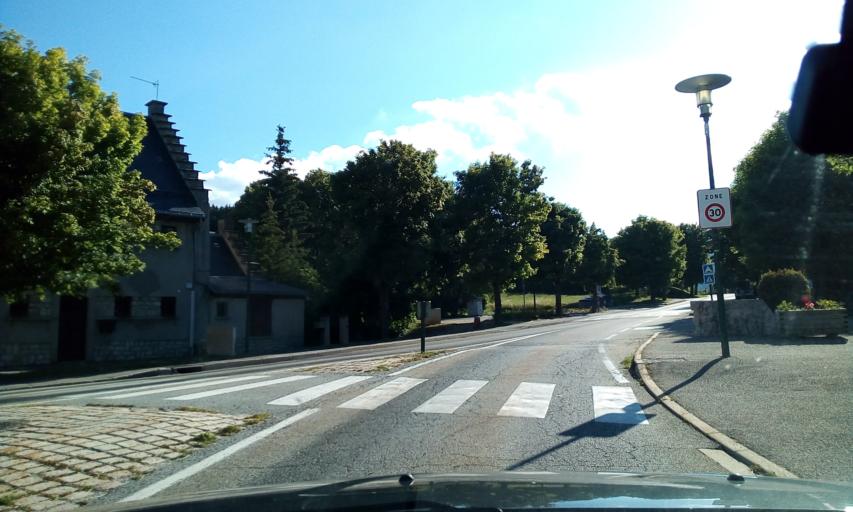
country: FR
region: Rhone-Alpes
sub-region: Departement de l'Isere
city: Sassenage
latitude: 45.1708
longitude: 5.6296
